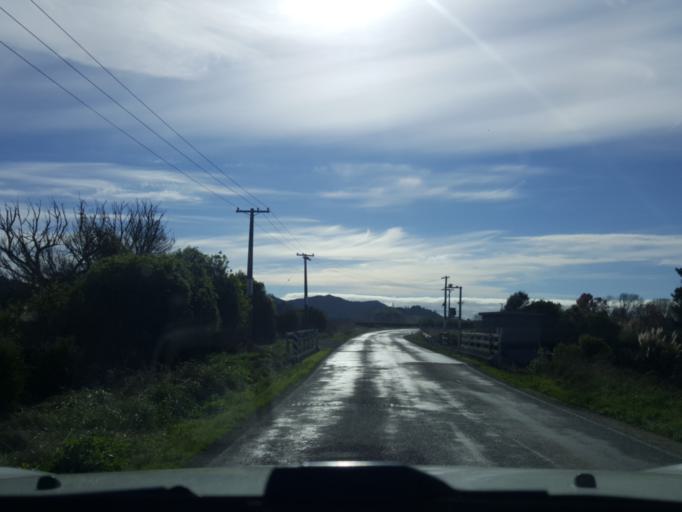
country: NZ
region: Waikato
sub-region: Waikato District
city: Ngaruawahia
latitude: -37.6068
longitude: 175.1980
